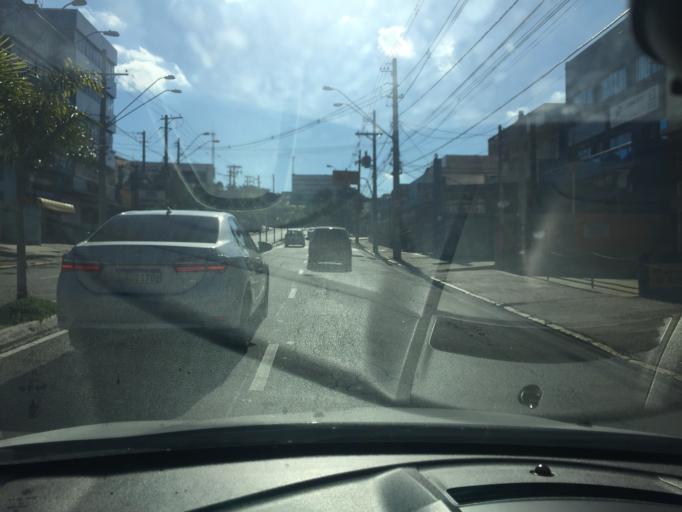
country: BR
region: Sao Paulo
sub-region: Varzea Paulista
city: Varzea Paulista
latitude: -23.2129
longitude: -46.8409
